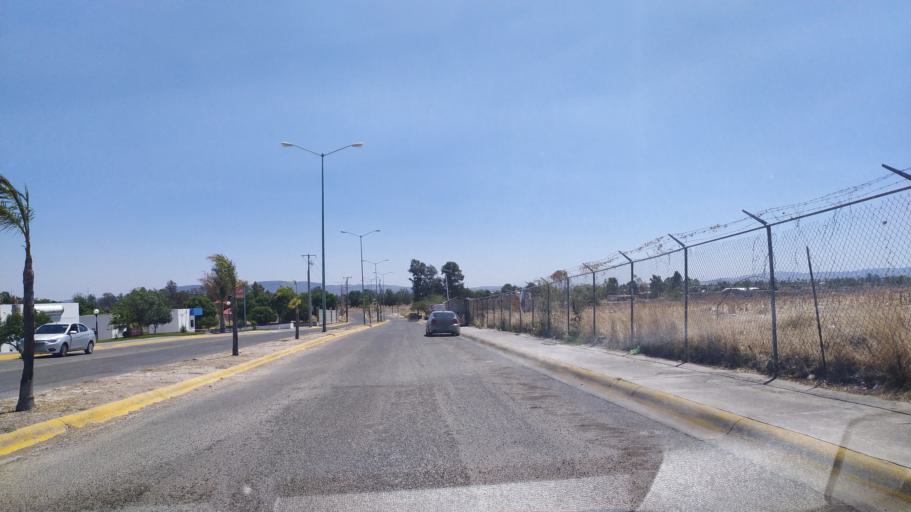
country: MX
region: Guanajuato
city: Ciudad Manuel Doblado
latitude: 20.7558
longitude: -101.9676
